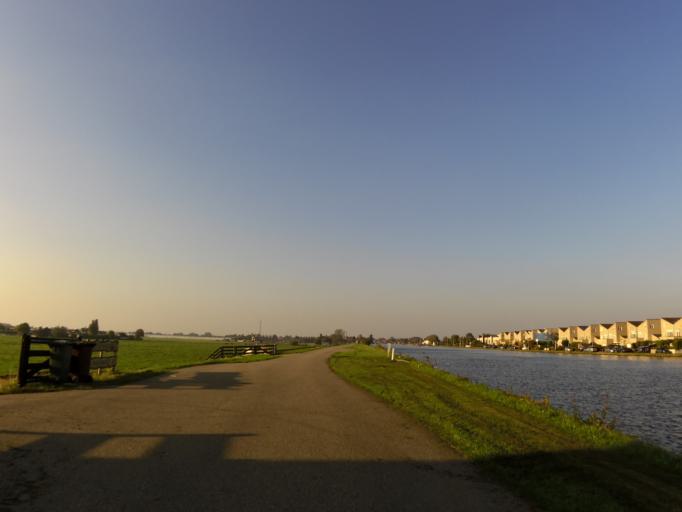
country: NL
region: South Holland
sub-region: Gemeente Alphen aan den Rijn
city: Alphen aan den Rijn
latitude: 52.1545
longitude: 4.6433
